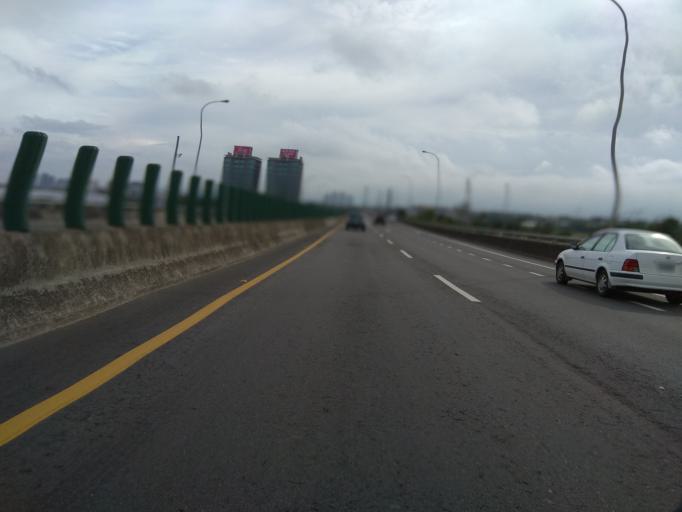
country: TW
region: Taiwan
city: Daxi
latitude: 24.8985
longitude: 121.2562
